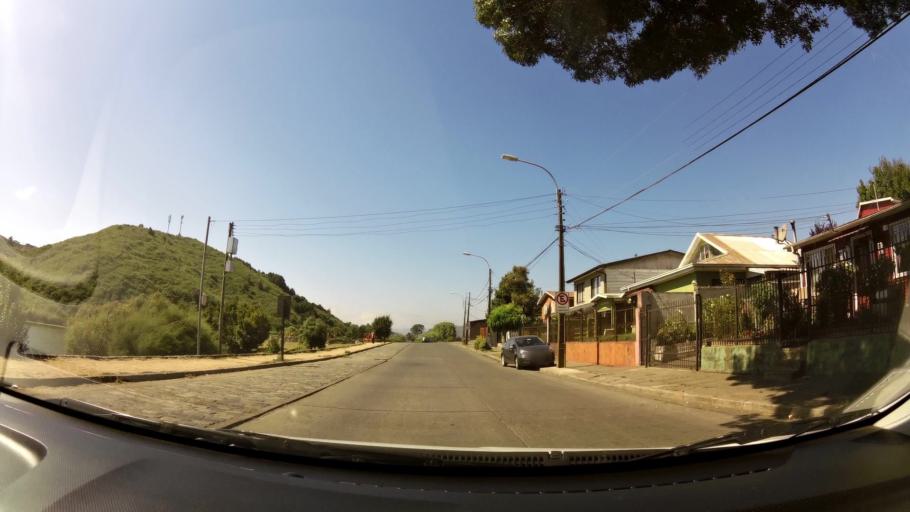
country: CL
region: Biobio
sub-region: Provincia de Concepcion
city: Concepcion
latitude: -36.8001
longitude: -73.0407
